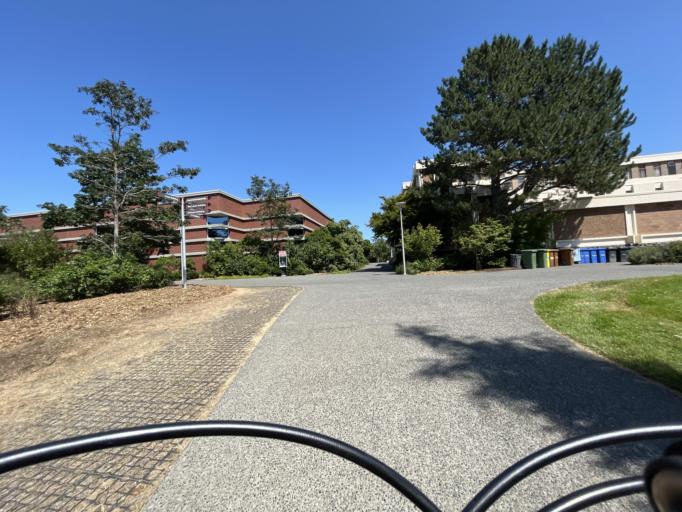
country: CA
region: British Columbia
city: Oak Bay
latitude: 48.4645
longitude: -123.3140
